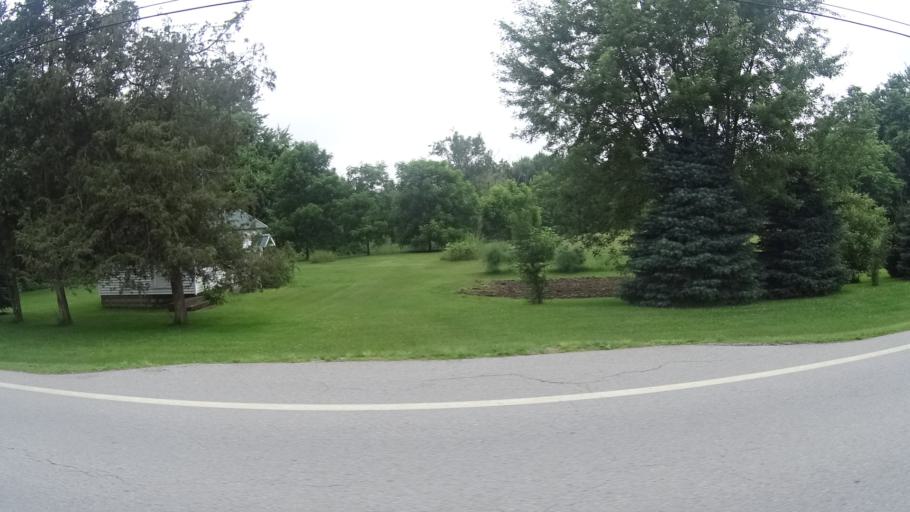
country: US
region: Ohio
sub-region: Erie County
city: Milan
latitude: 41.2912
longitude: -82.5325
